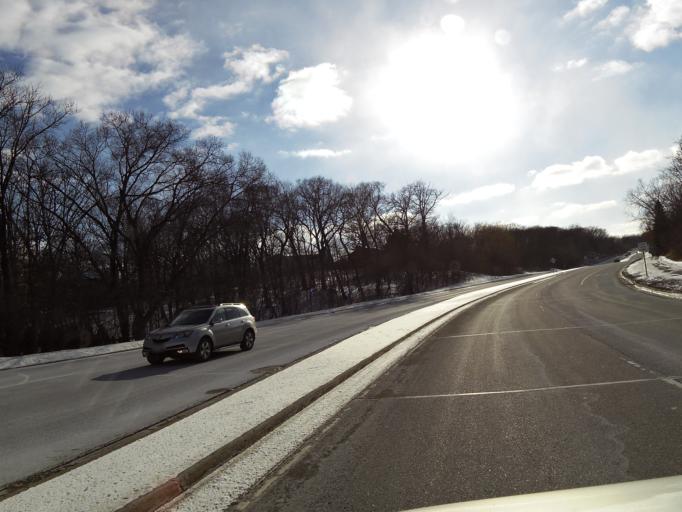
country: US
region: Minnesota
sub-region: Dakota County
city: Apple Valley
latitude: 44.7580
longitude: -93.2237
